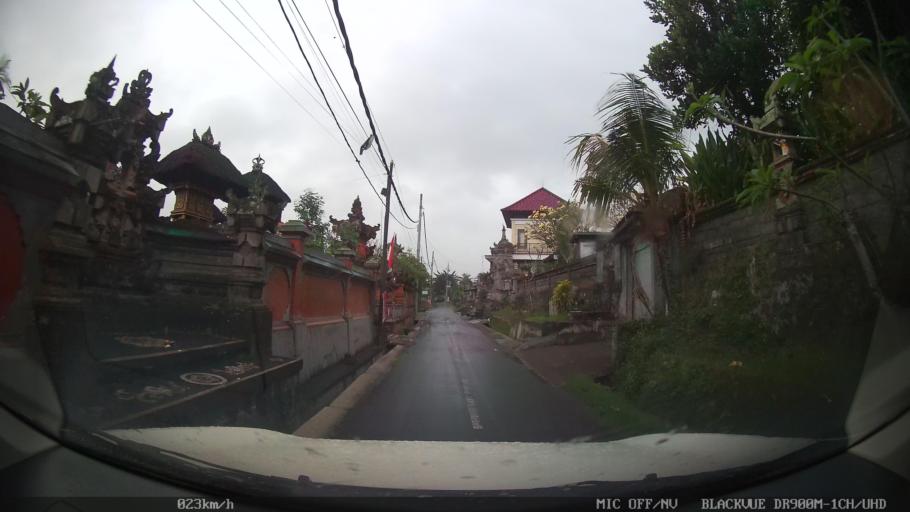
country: ID
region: Bali
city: Banjar Sedang
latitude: -8.5728
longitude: 115.2559
